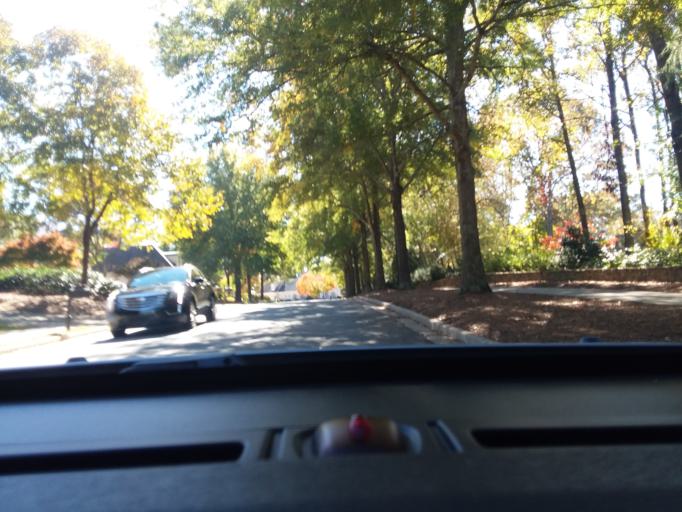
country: US
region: Georgia
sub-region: Fulton County
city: Johns Creek
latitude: 34.0309
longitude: -84.1742
